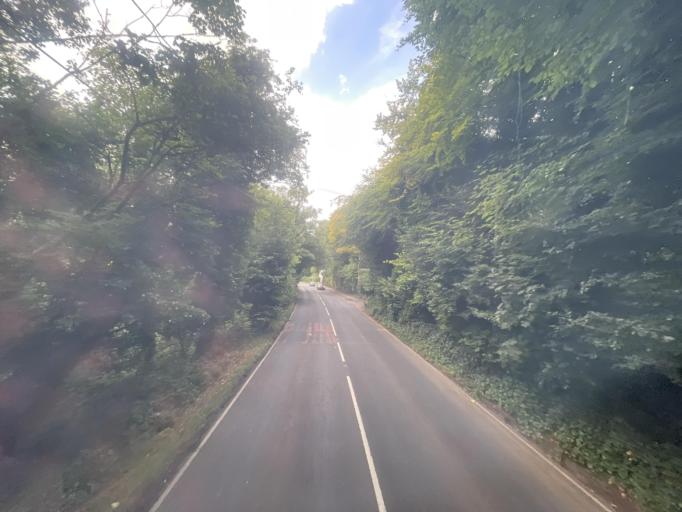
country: GB
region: England
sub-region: Kent
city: Westerham
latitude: 51.2852
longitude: 0.0644
